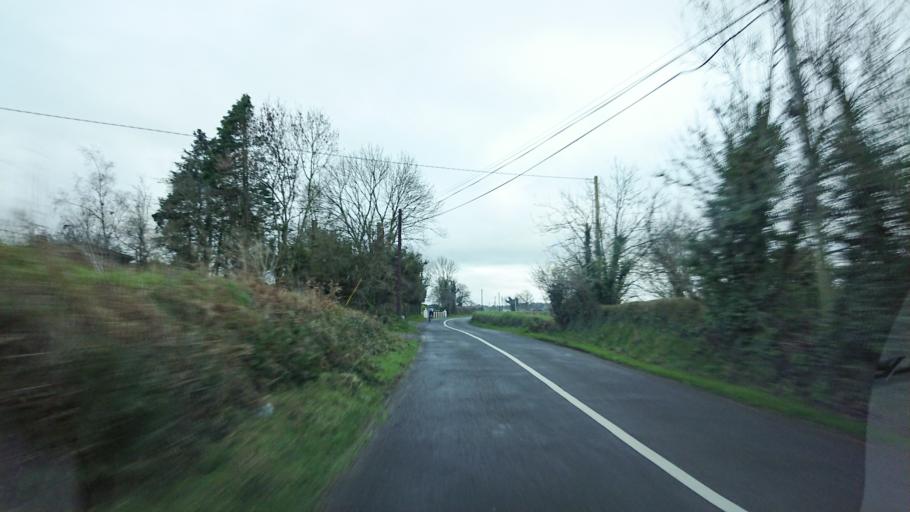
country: IE
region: Munster
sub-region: Waterford
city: Portlaw
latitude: 52.1857
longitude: -7.4086
